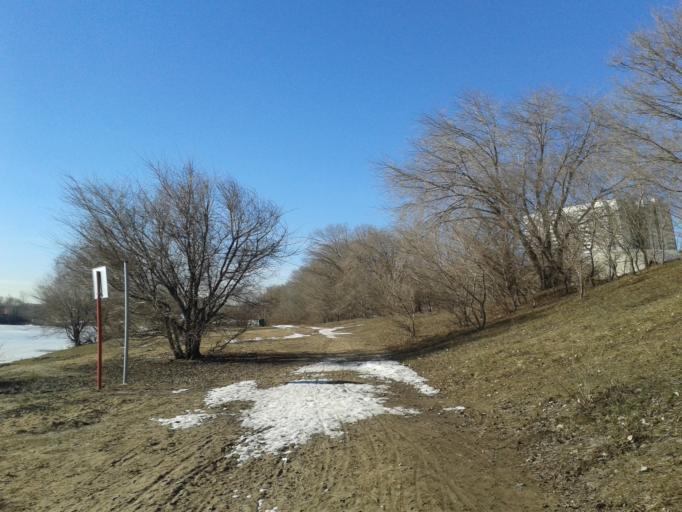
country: RU
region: Moscow
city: Strogino
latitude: 55.8005
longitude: 37.4169
